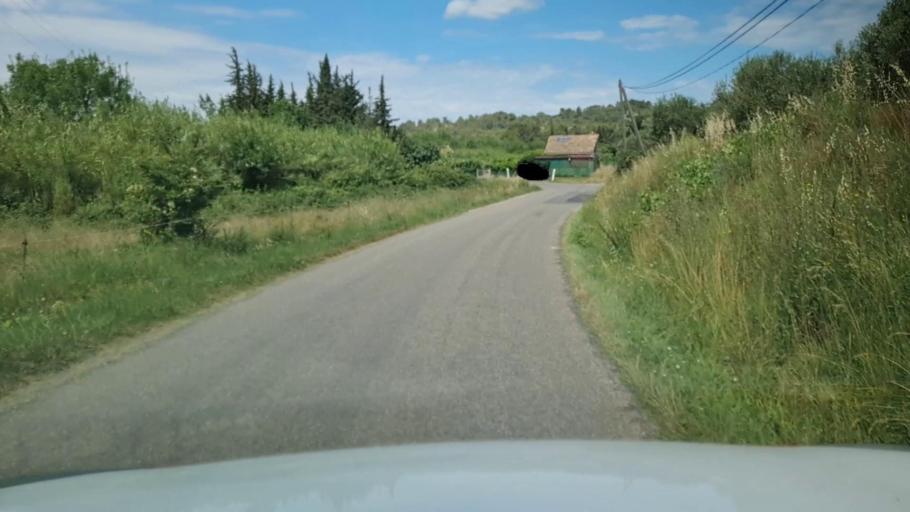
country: FR
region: Languedoc-Roussillon
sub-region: Departement du Gard
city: Clarensac
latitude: 43.8266
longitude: 4.1884
